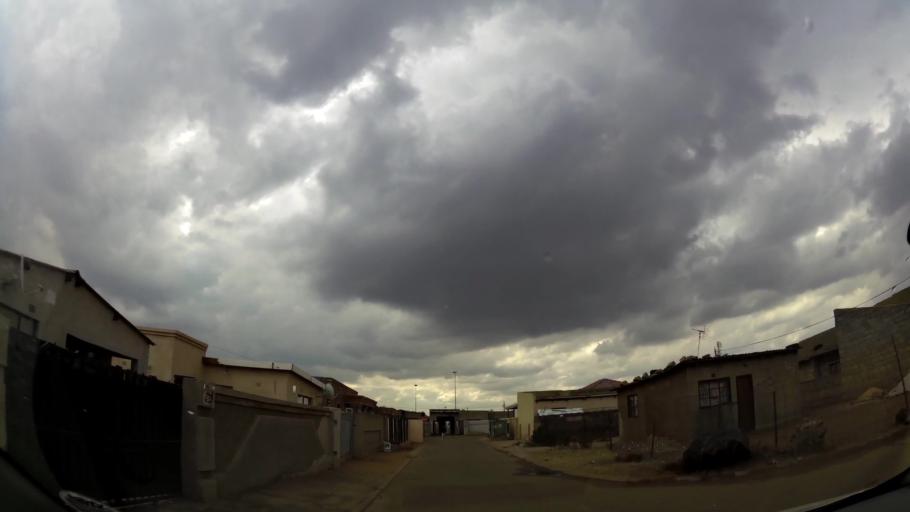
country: ZA
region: Gauteng
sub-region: Ekurhuleni Metropolitan Municipality
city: Germiston
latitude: -26.3689
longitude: 28.1601
